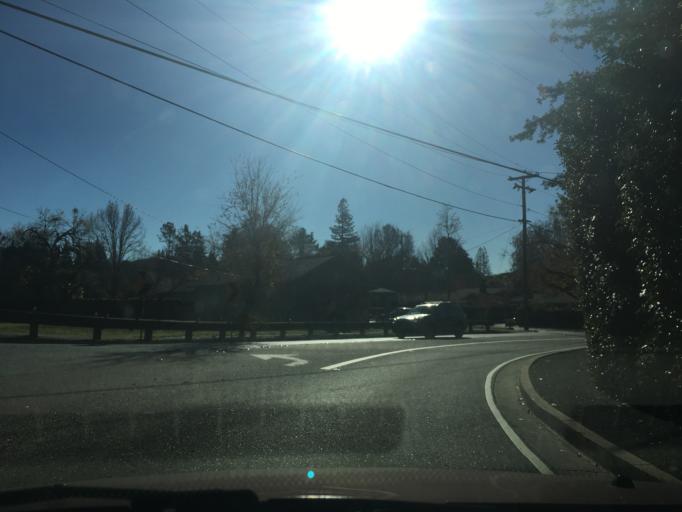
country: US
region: California
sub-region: Contra Costa County
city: Saranap
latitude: 37.8750
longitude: -122.0946
